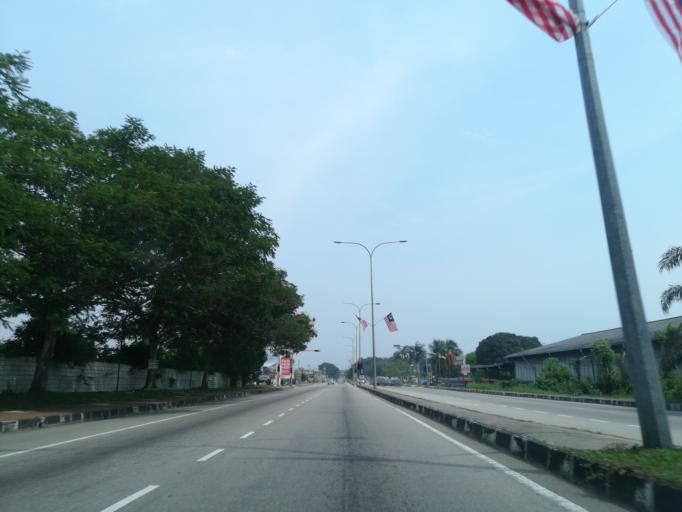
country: MY
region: Kedah
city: Kulim
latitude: 5.4102
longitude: 100.5471
